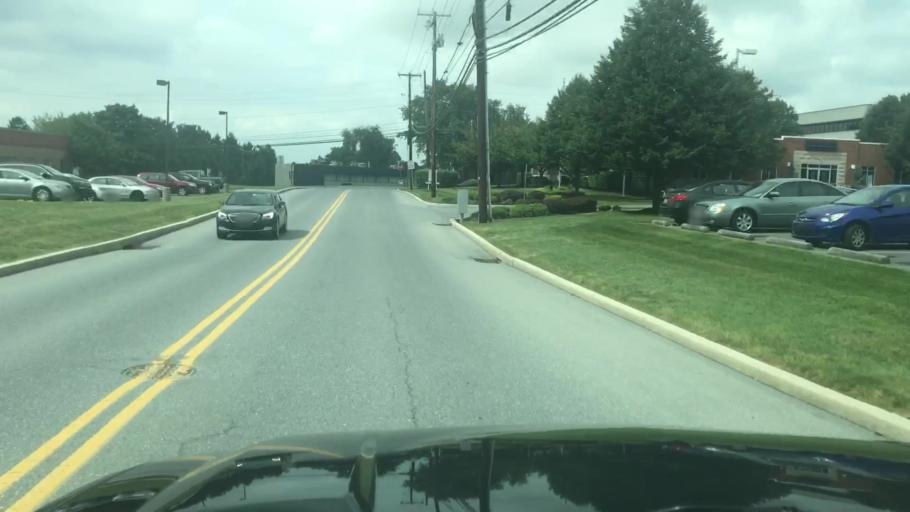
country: US
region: Pennsylvania
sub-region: Dauphin County
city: Progress
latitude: 40.3112
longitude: -76.8429
